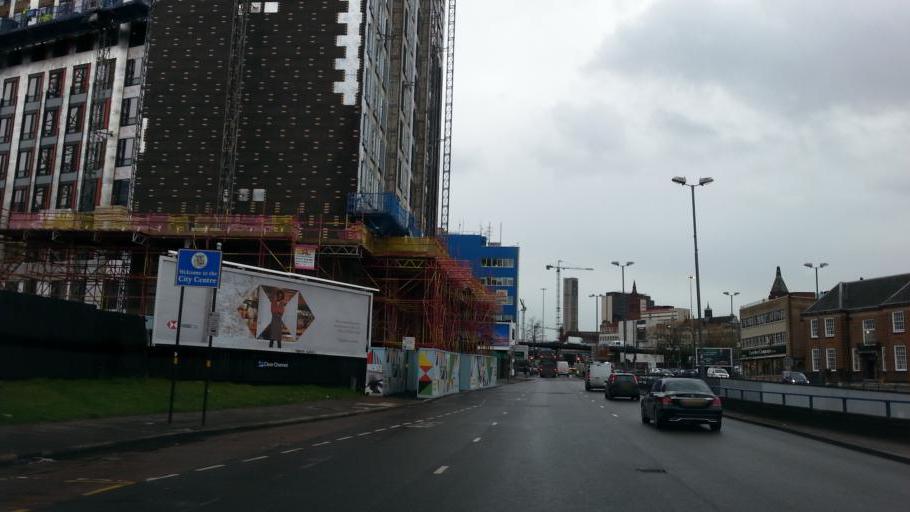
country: GB
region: England
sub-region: City and Borough of Birmingham
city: Birmingham
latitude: 52.4882
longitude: -1.8936
